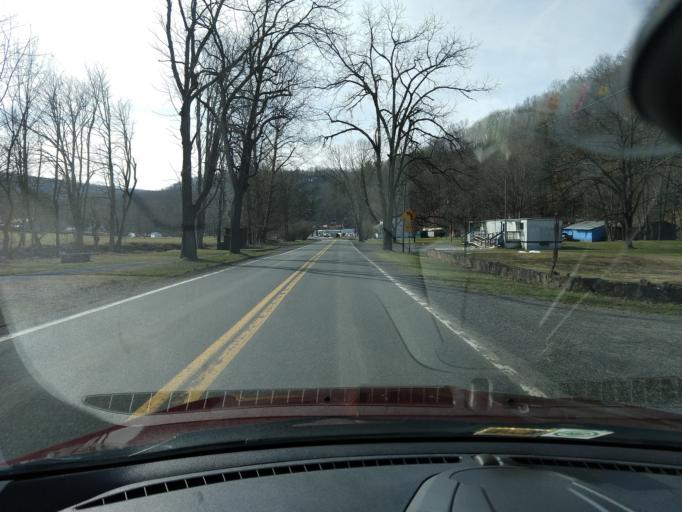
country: US
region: West Virginia
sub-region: Pocahontas County
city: Marlinton
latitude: 38.1891
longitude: -80.1352
